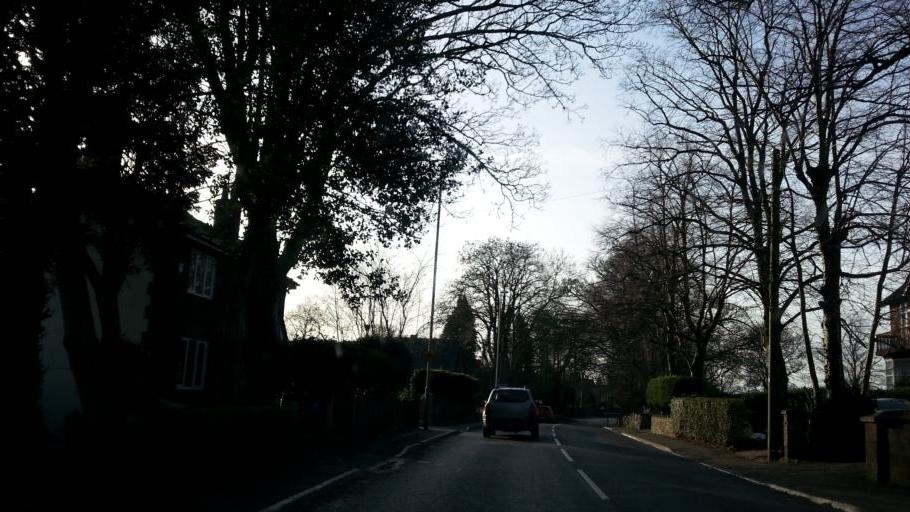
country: GB
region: England
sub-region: Staffordshire
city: Biddulph
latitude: 53.0680
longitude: -2.1196
